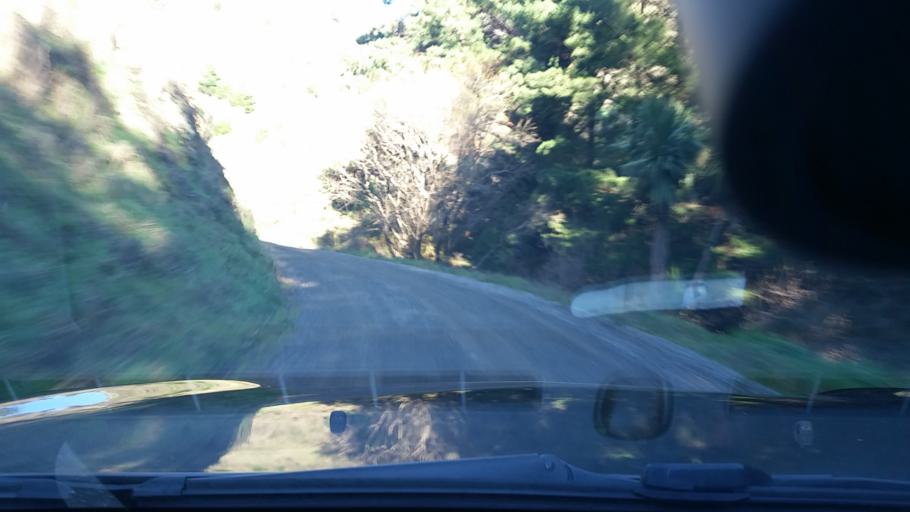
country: NZ
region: Marlborough
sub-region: Marlborough District
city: Blenheim
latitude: -41.6277
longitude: 173.9699
